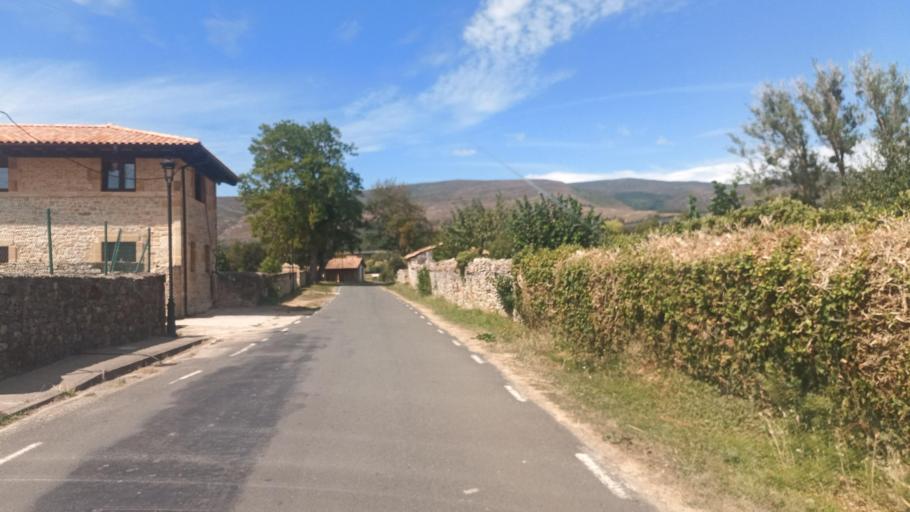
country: ES
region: Castille and Leon
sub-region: Provincia de Burgos
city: Espinosa de los Monteros
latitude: 43.0410
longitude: -3.6670
